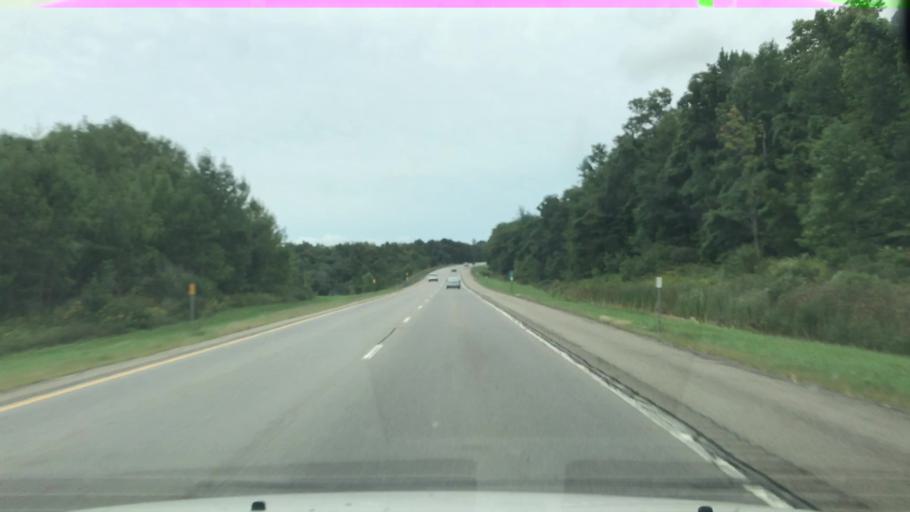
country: US
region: New York
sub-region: Erie County
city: Springville
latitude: 42.5769
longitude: -78.7216
